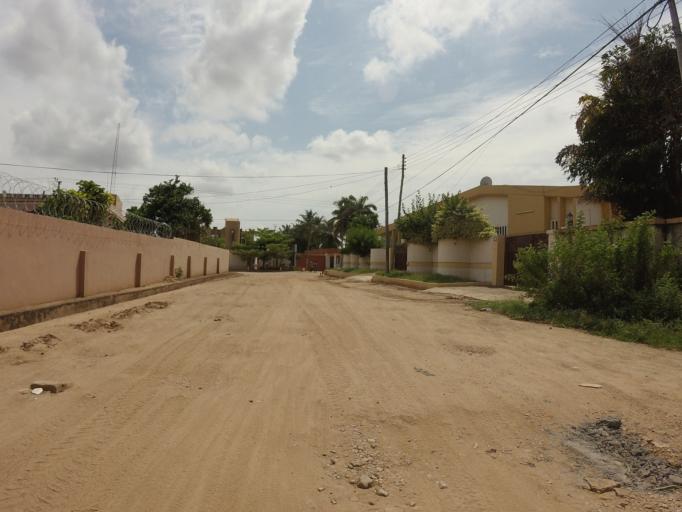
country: GH
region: Greater Accra
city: Dome
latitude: 5.6379
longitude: -0.2346
